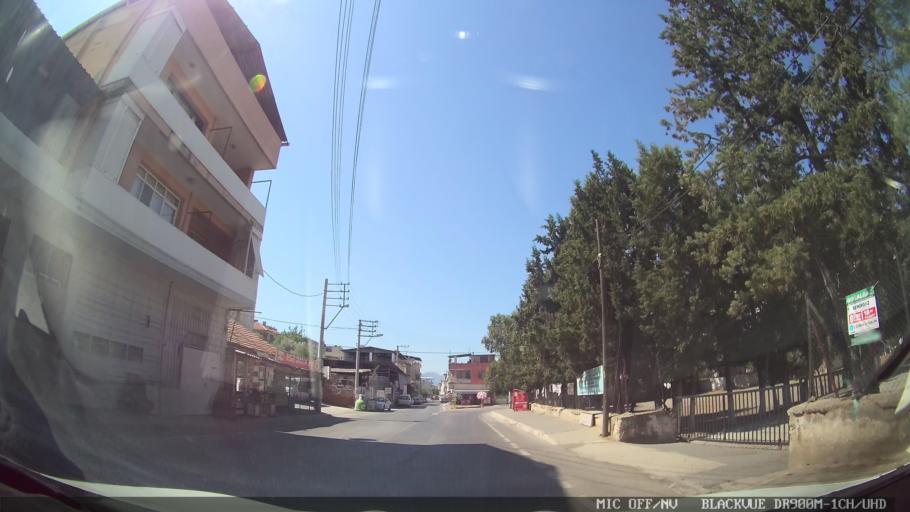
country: TR
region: Izmir
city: Karsiyaka
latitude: 38.4983
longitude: 27.0685
